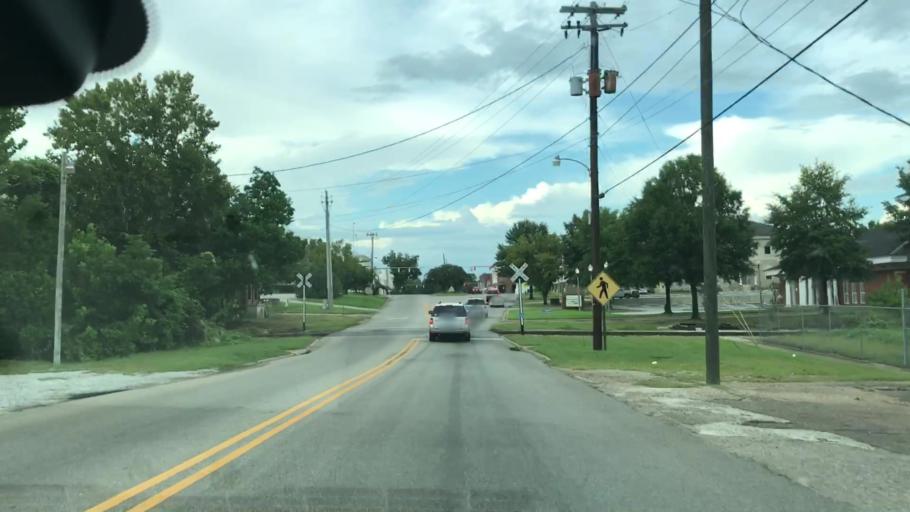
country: US
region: Alabama
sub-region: Barbour County
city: Eufaula
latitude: 31.8896
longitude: -85.1439
